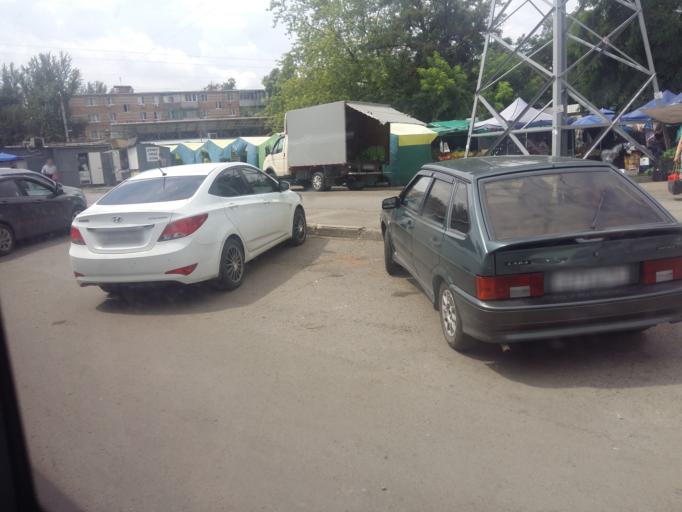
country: RU
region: Rostov
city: Imeni Chkalova
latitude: 47.2836
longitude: 39.7574
